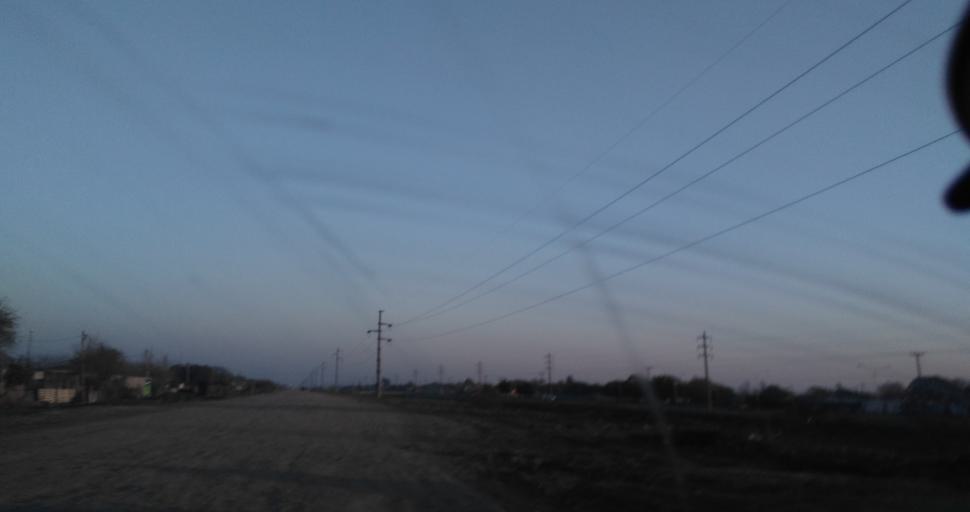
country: AR
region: Chaco
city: Resistencia
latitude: -27.4866
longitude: -58.9911
